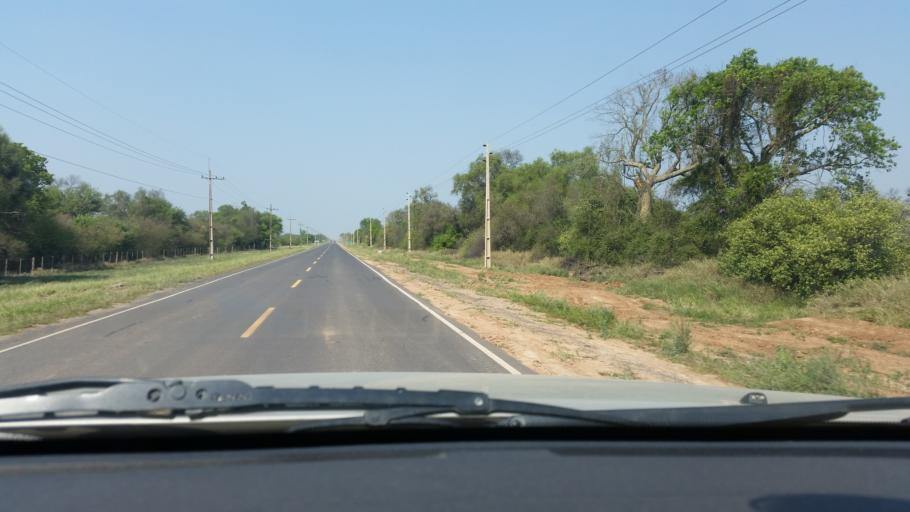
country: PY
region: Boqueron
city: Colonia Neuland
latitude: -22.6047
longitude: -60.1051
